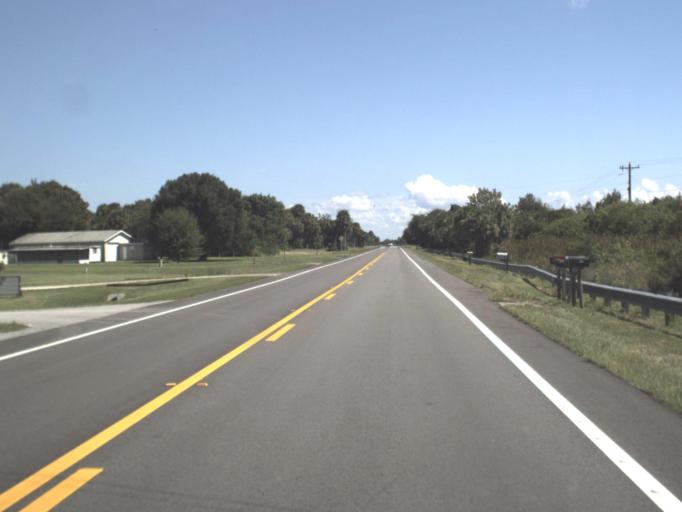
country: US
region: Florida
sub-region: Glades County
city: Moore Haven
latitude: 27.0059
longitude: -81.0505
